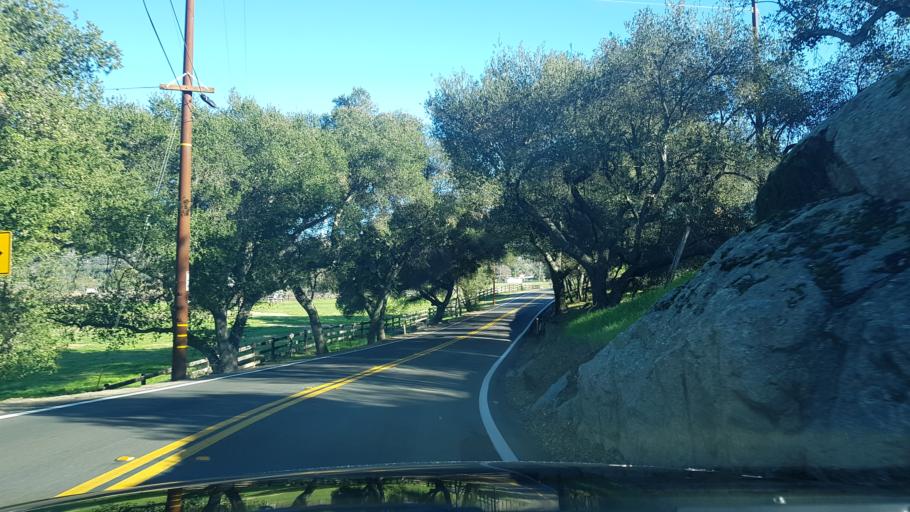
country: US
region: California
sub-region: San Diego County
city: Valley Center
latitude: 33.2056
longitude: -116.9778
